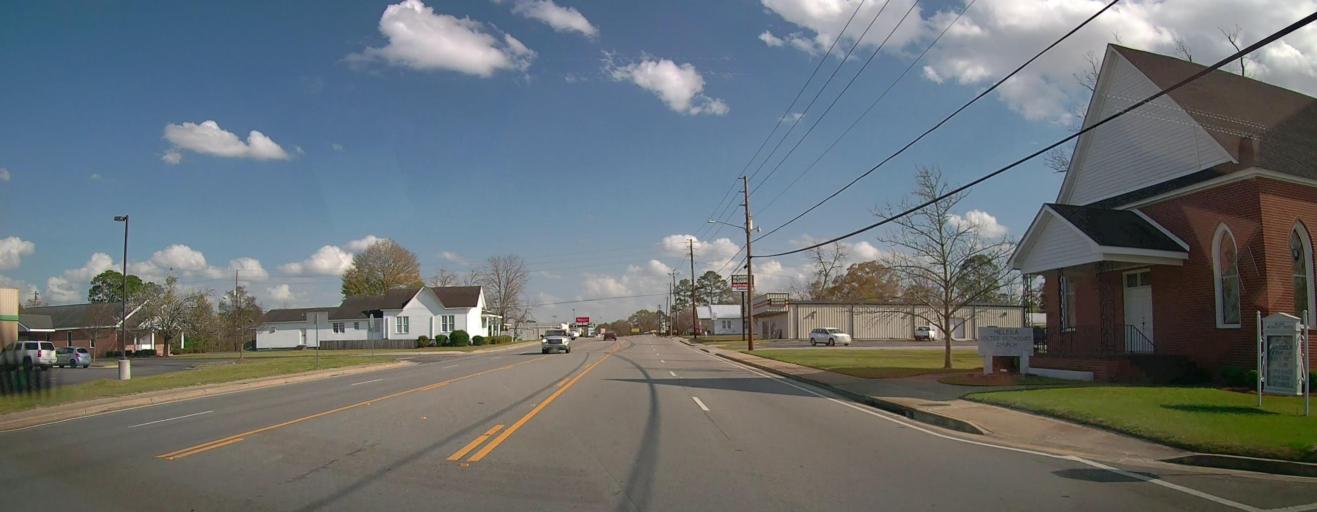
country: US
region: Georgia
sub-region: Telfair County
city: Helena
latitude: 32.0723
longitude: -82.9123
